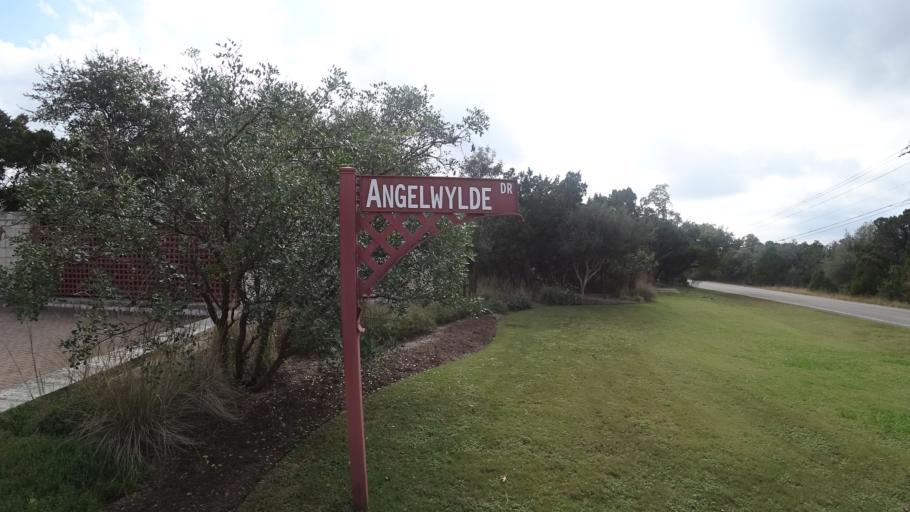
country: US
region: Texas
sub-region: Travis County
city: Barton Creek
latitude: 30.3098
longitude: -97.8803
